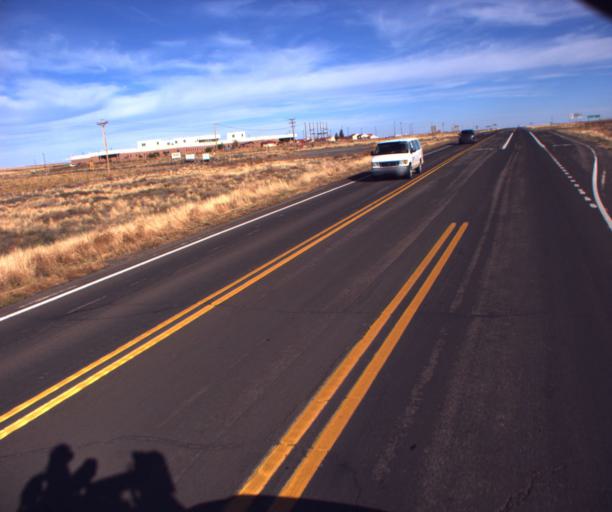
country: US
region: Arizona
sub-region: Apache County
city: Lukachukai
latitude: 36.9598
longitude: -109.3534
